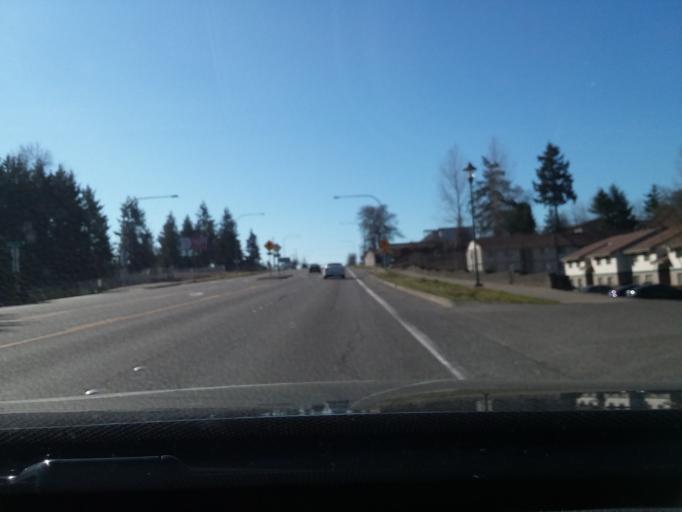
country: US
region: Washington
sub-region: Pierce County
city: Spanaway
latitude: 47.1278
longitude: -122.4349
